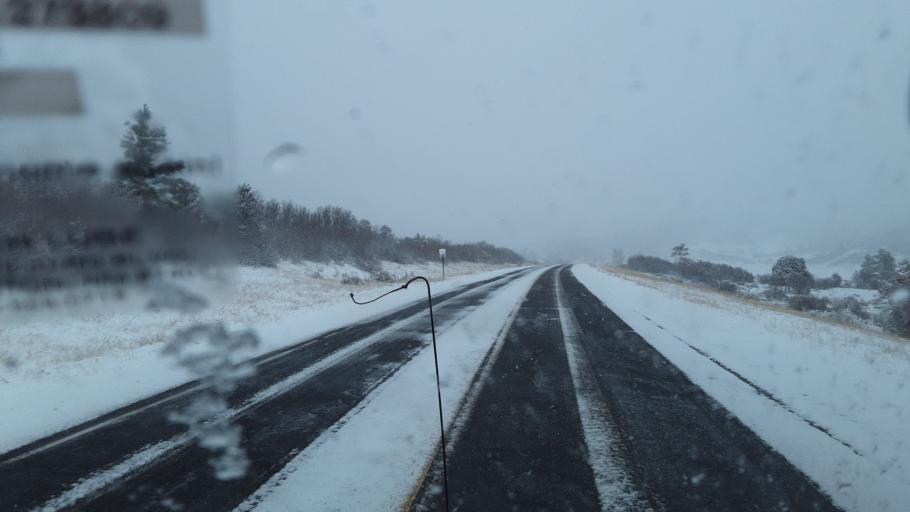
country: US
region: New Mexico
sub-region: Rio Arriba County
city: Dulce
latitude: 36.9577
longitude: -106.7870
